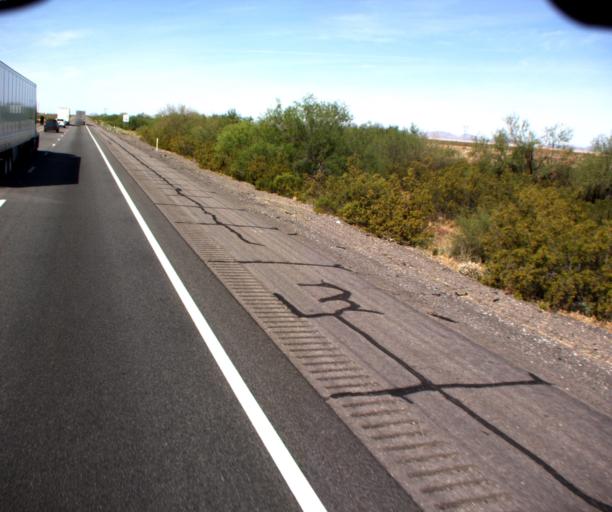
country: US
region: Arizona
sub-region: La Paz County
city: Salome
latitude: 33.5712
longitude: -113.3658
